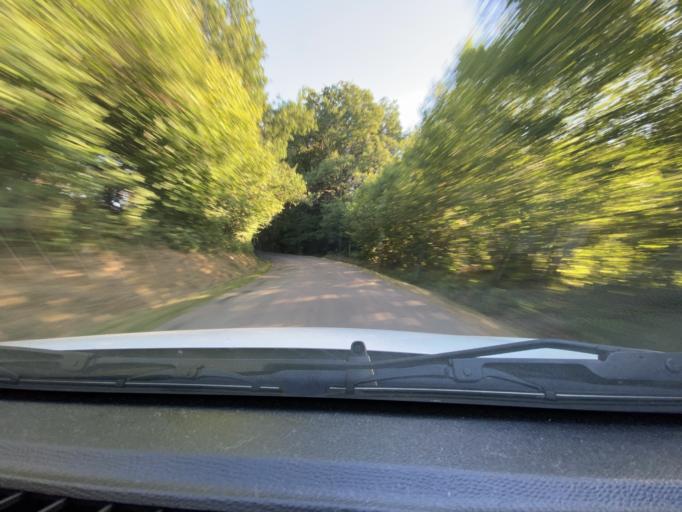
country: FR
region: Bourgogne
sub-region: Departement de la Cote-d'Or
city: Saulieu
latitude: 47.2916
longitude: 4.1701
